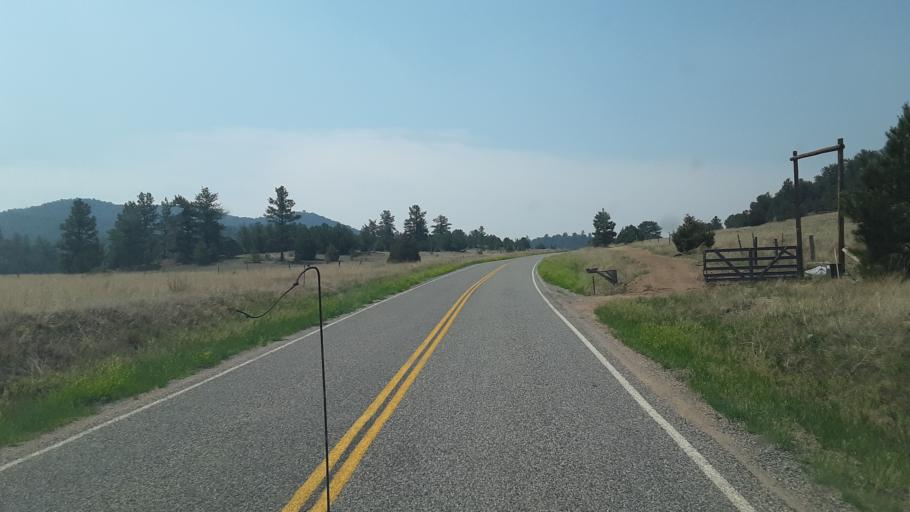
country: US
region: Colorado
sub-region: Fremont County
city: Canon City
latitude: 38.3776
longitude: -105.4562
